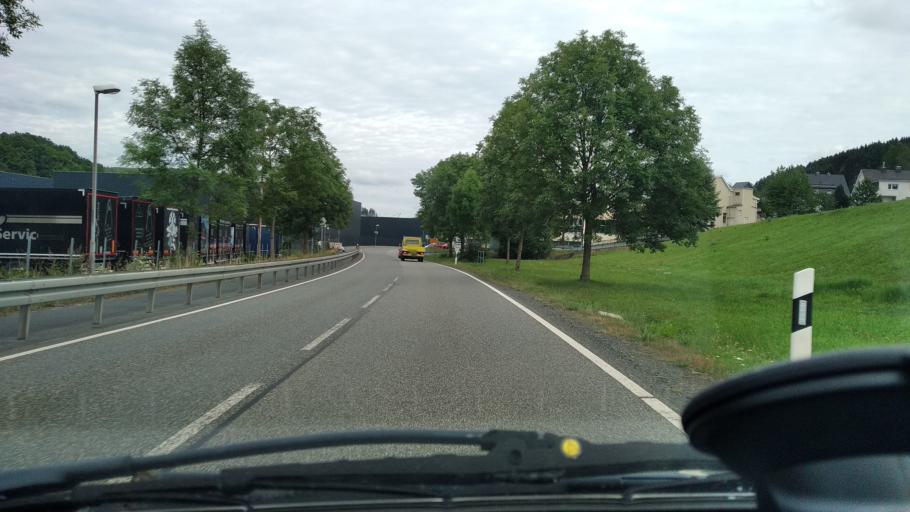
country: DE
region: Hesse
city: Dillenburg
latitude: 50.8369
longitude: 8.2985
